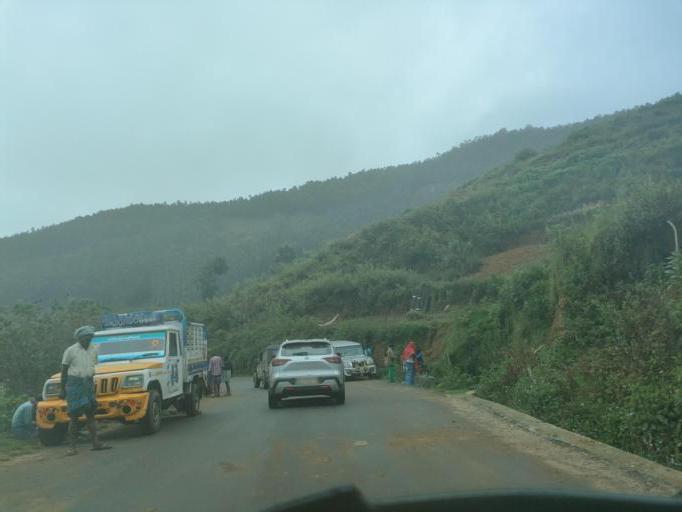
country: IN
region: Tamil Nadu
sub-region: Dindigul
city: Kodaikanal
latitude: 10.2394
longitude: 77.3511
